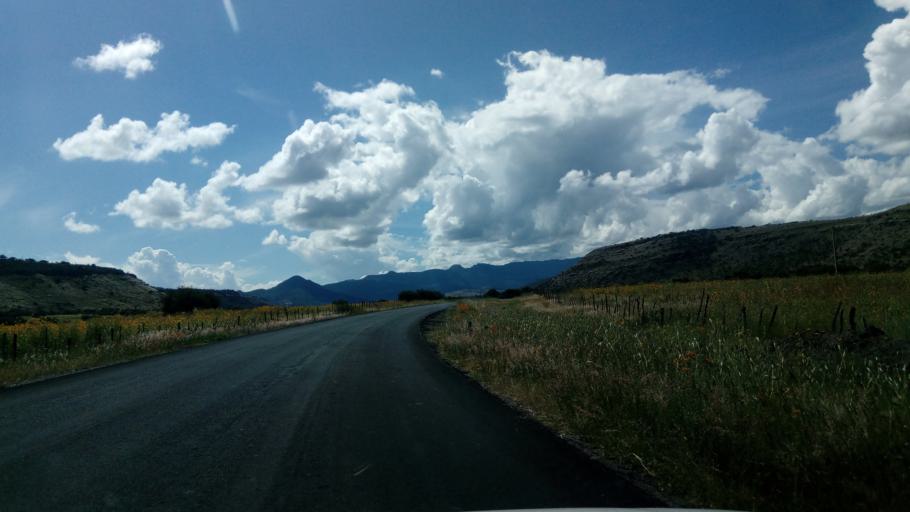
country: MX
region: Durango
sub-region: Durango
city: Jose Refugio Salcido
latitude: 23.8263
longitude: -104.4819
